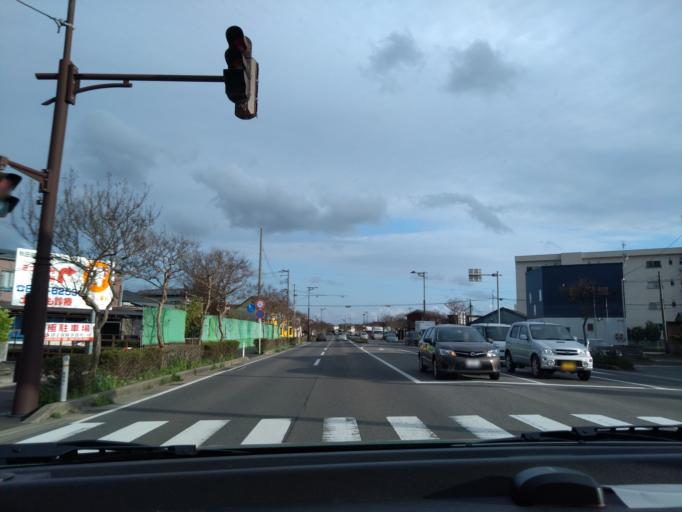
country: JP
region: Akita
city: Akita Shi
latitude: 39.7592
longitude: 140.0910
